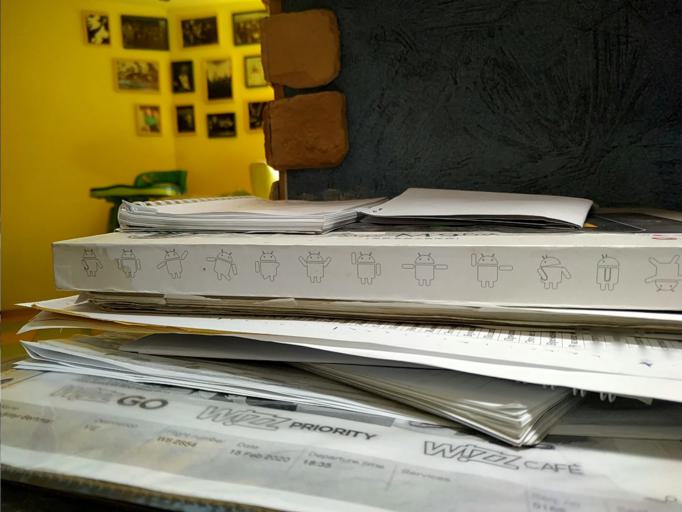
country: RU
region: Novgorod
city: Utorgosh
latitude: 58.1348
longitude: 30.0624
